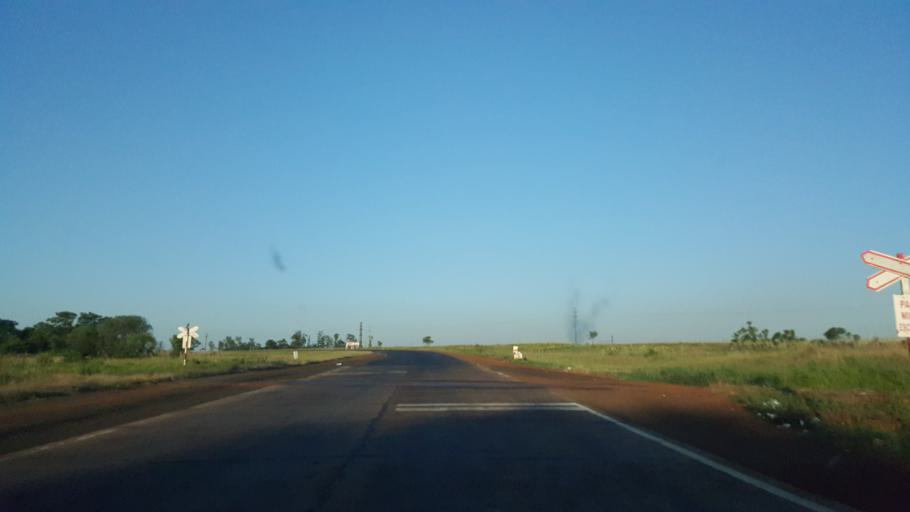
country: AR
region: Corrientes
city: Santo Tome
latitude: -28.3573
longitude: -56.1124
